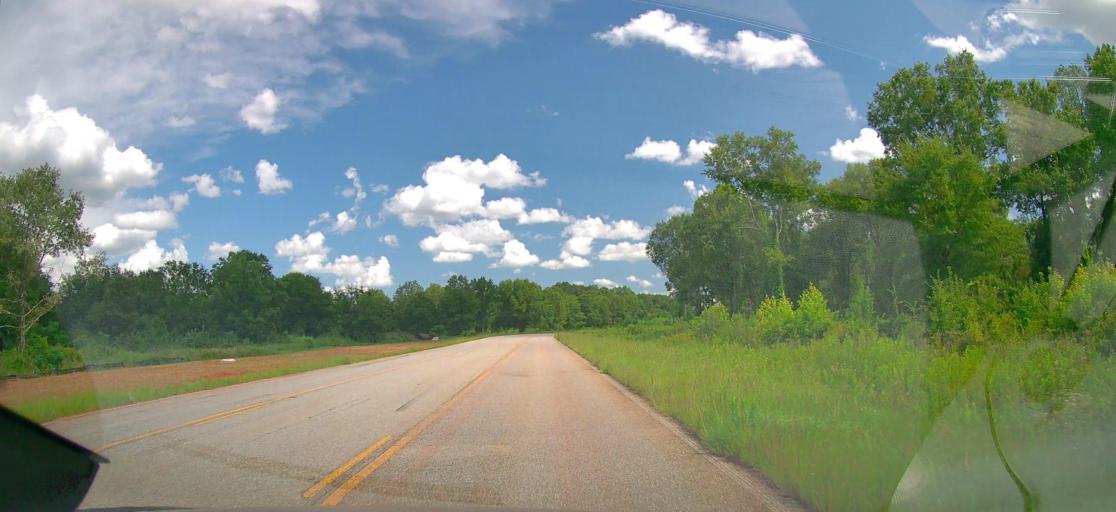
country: US
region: Georgia
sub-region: Houston County
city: Centerville
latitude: 32.5972
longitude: -83.7397
